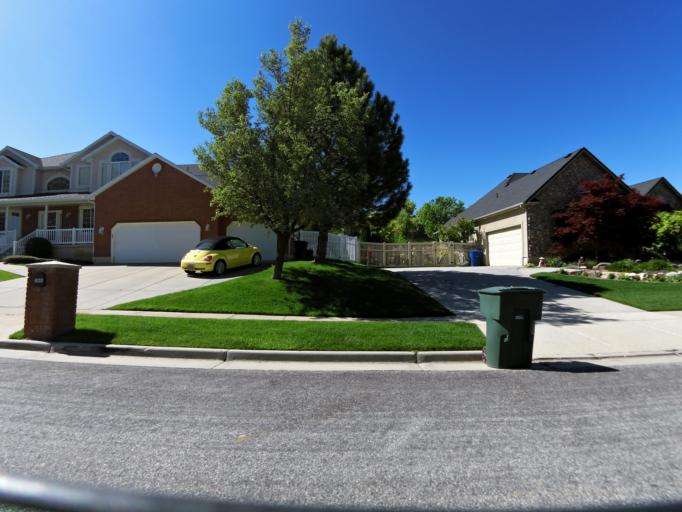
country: US
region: Utah
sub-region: Weber County
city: Uintah
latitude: 41.1647
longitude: -111.9317
